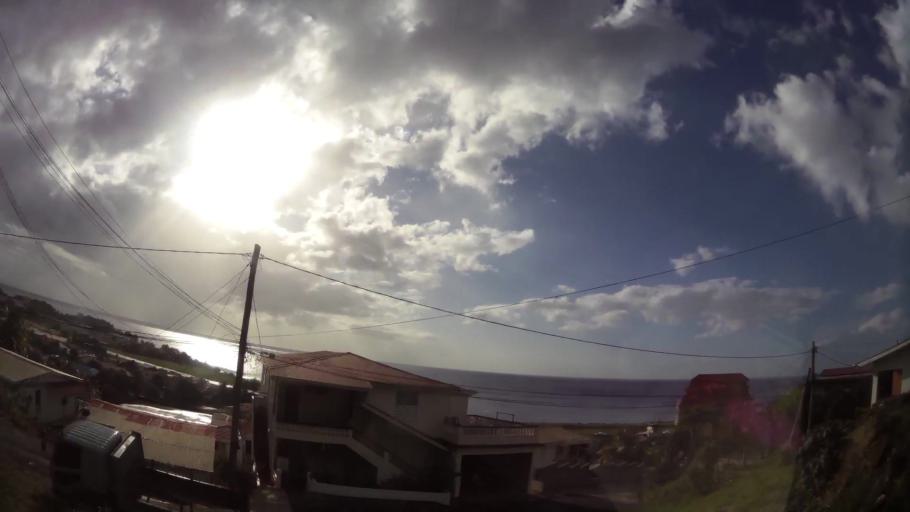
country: DM
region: Saint Paul
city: Mahaut
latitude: 15.3381
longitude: -61.3893
